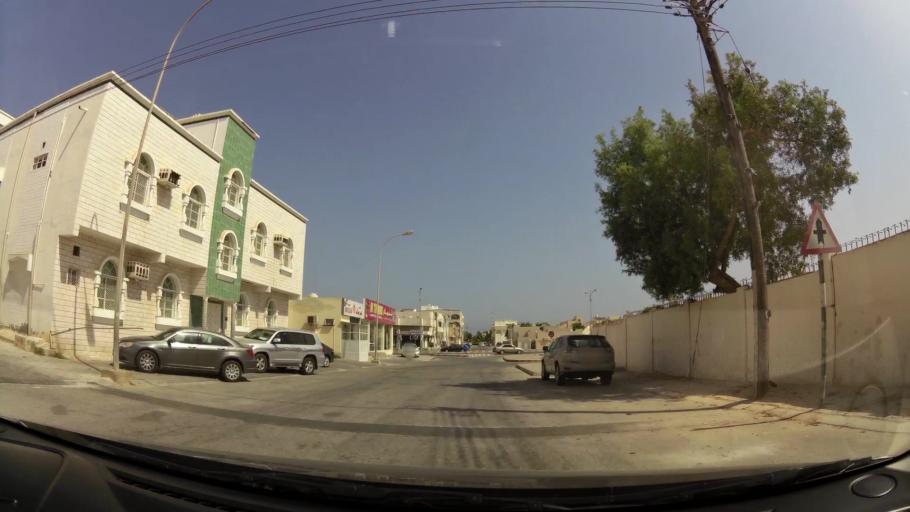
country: OM
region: Zufar
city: Salalah
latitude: 17.0063
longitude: 54.0625
